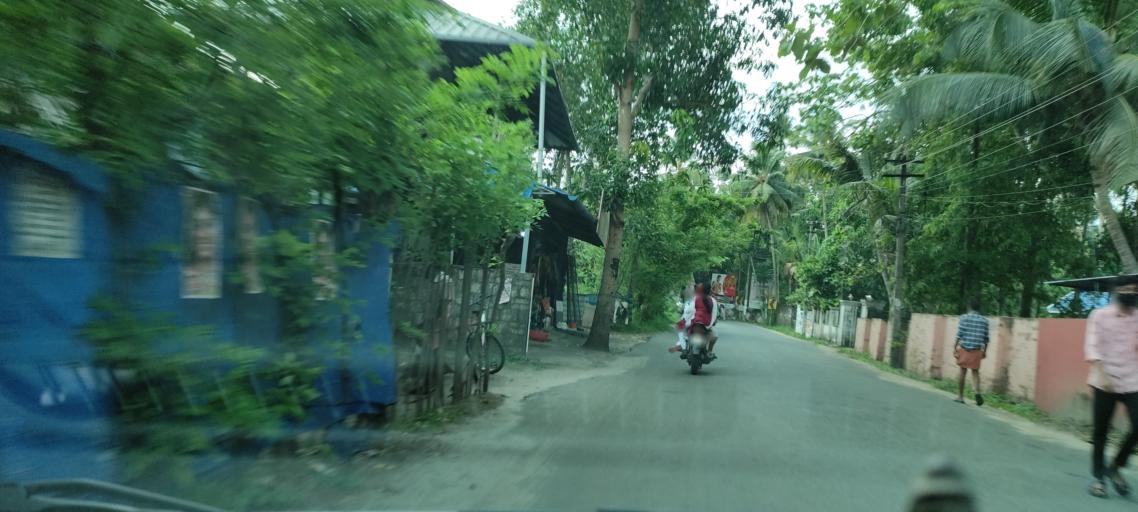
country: IN
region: Kerala
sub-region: Alappuzha
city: Kutiatodu
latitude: 9.8205
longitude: 76.3470
